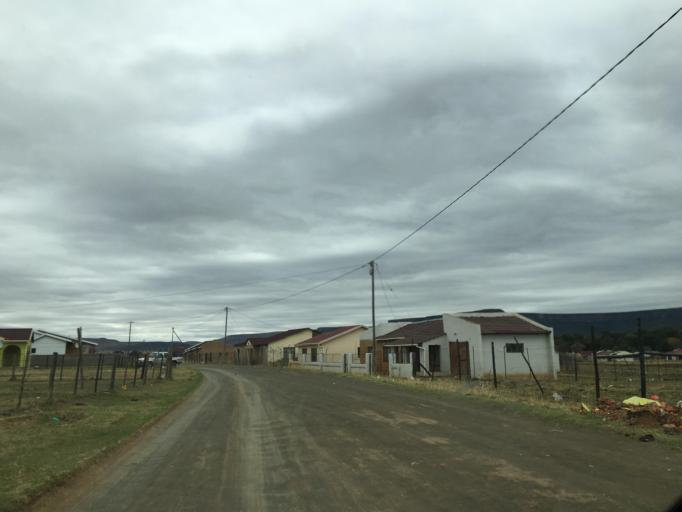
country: ZA
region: Eastern Cape
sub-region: Chris Hani District Municipality
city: Cala
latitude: -31.5340
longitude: 27.6945
